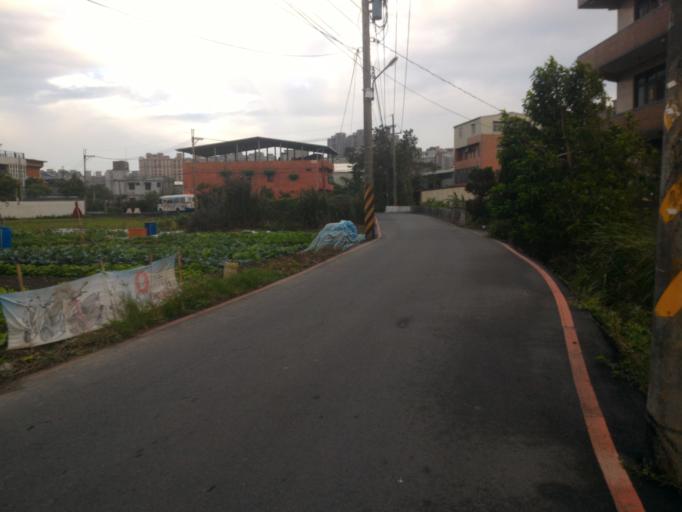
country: TW
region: Taiwan
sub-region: Taoyuan
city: Taoyuan
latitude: 24.9424
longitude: 121.3849
